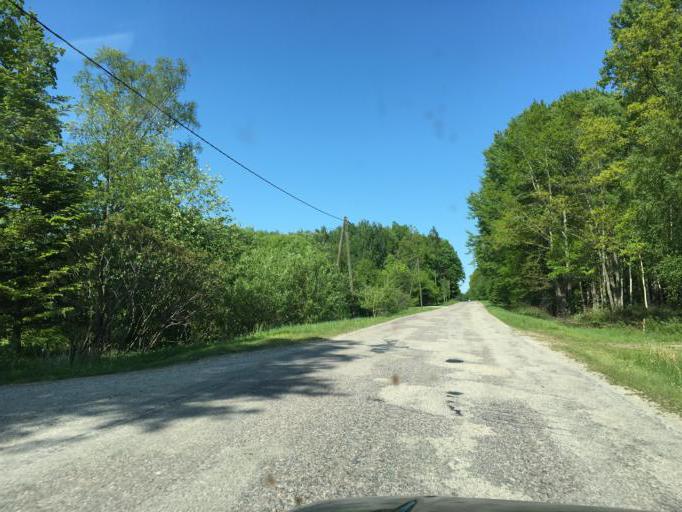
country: LV
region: Dundaga
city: Dundaga
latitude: 57.4949
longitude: 22.3451
